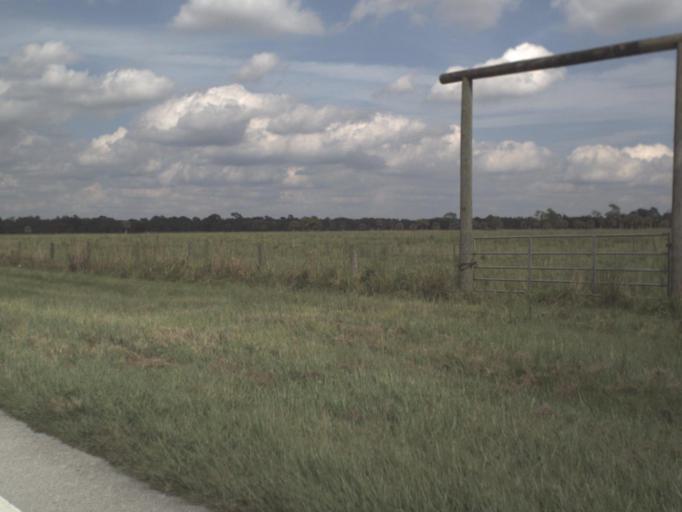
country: US
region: Florida
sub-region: Okeechobee County
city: Cypress Quarters
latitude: 27.3168
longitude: -80.8252
